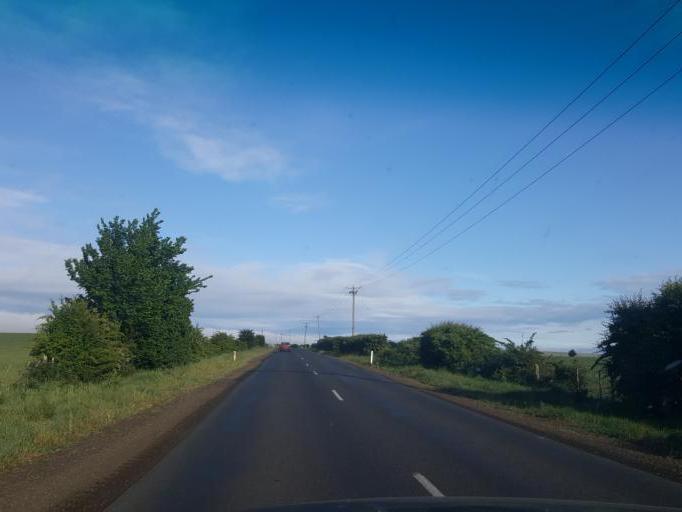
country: AU
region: Tasmania
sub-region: Northern Midlands
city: Evandale
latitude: -41.5642
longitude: 147.2337
